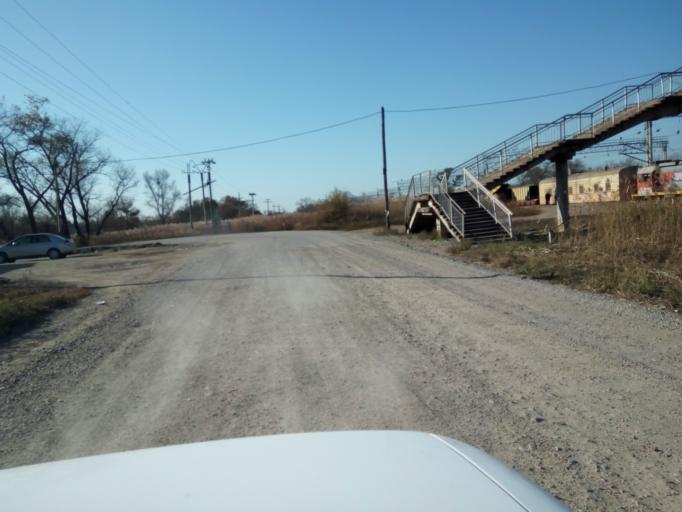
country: RU
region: Primorskiy
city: Lazo
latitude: 45.8767
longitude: 133.6466
